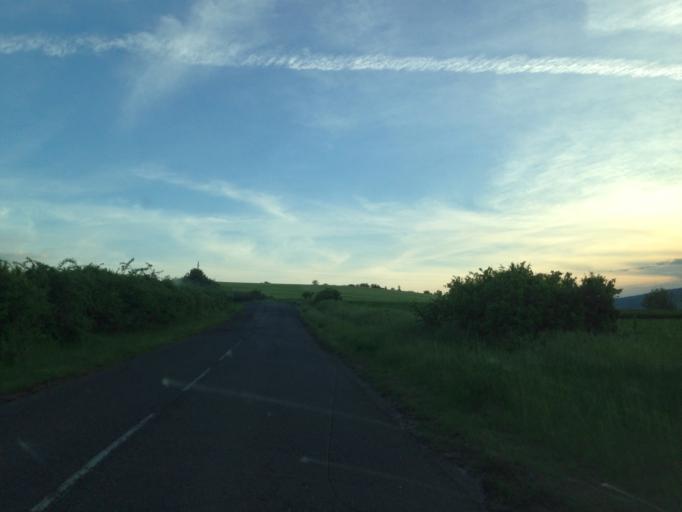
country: HU
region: Nograd
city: Tar
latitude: 47.9426
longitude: 19.7258
